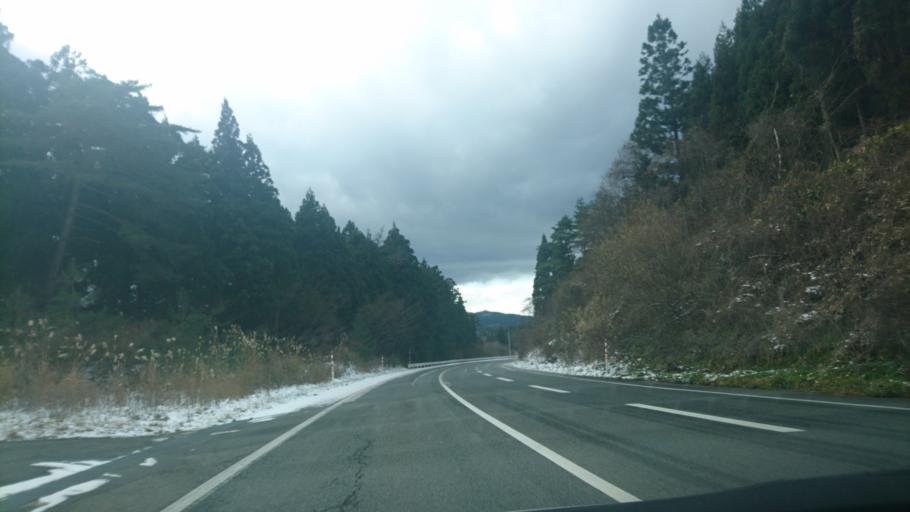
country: JP
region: Iwate
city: Mizusawa
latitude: 39.1721
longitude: 141.3338
